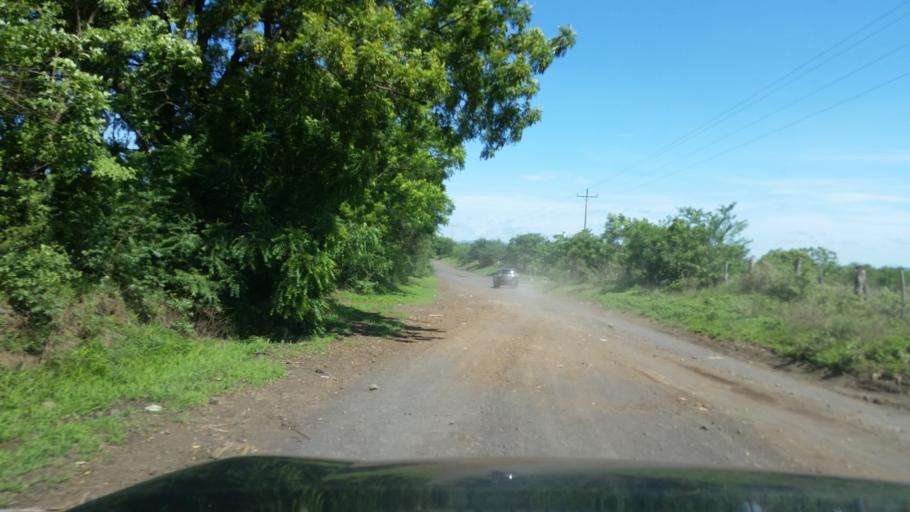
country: NI
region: Chinandega
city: Puerto Morazan
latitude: 12.7682
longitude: -87.0649
